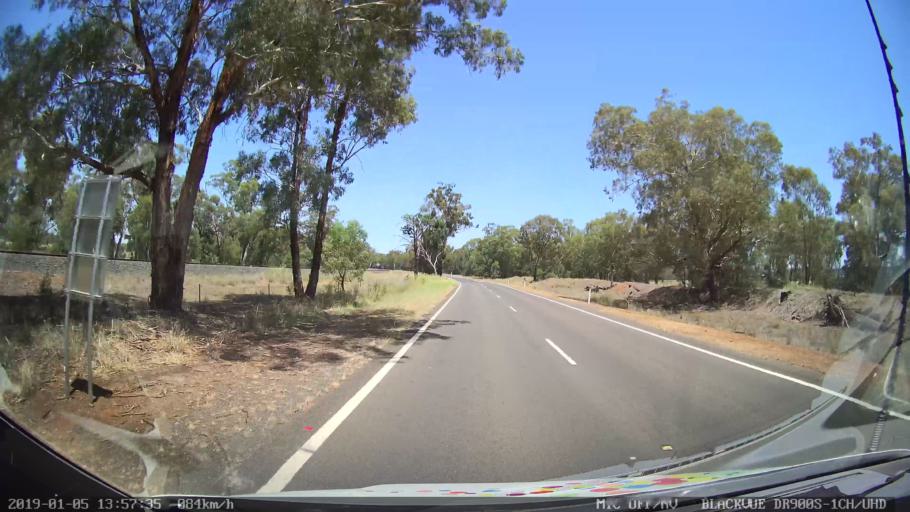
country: AU
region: New South Wales
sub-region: Gunnedah
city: Gunnedah
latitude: -31.1292
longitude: 150.2754
